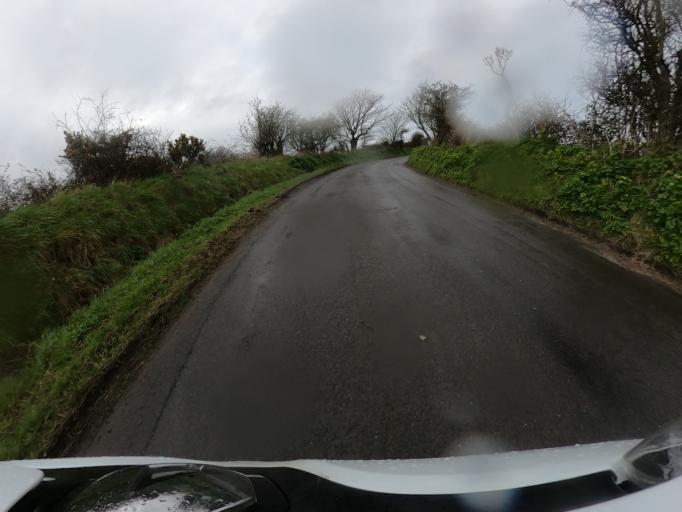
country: IM
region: Ramsey
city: Ramsey
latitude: 54.3724
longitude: -4.4491
